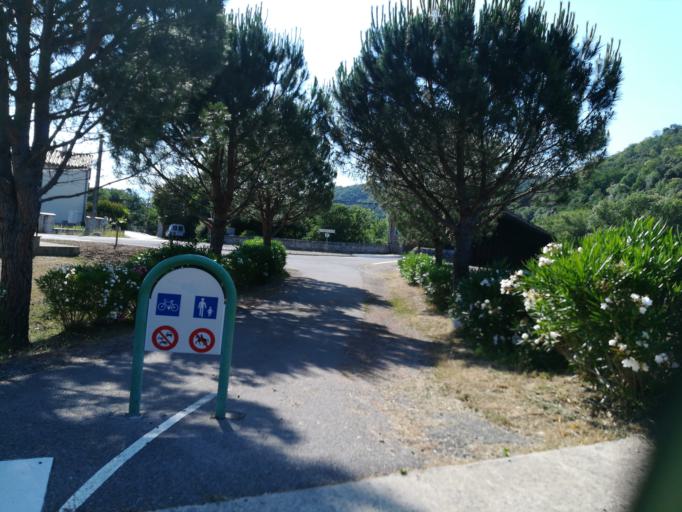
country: FR
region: Languedoc-Roussillon
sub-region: Departement des Pyrenees-Orientales
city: Reiners
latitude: 42.4953
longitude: 2.7181
